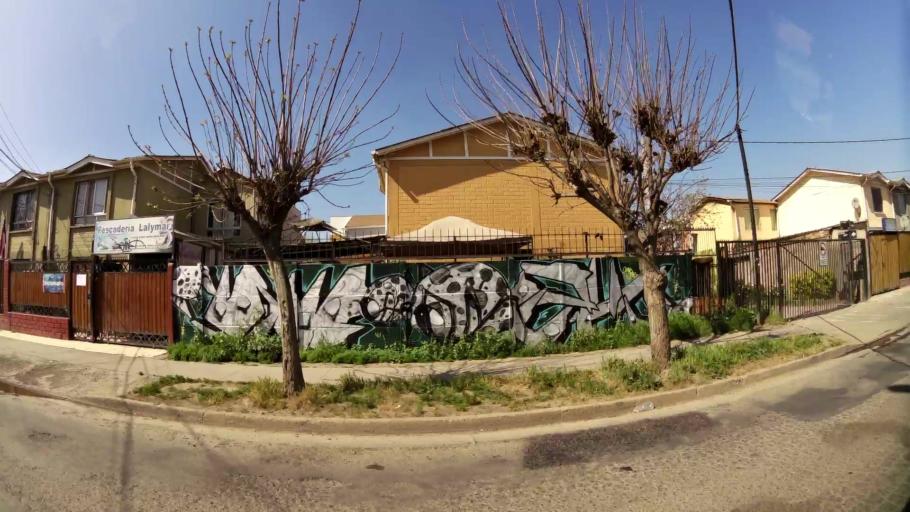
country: CL
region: Santiago Metropolitan
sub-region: Provincia de Santiago
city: Lo Prado
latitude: -33.3543
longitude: -70.7463
